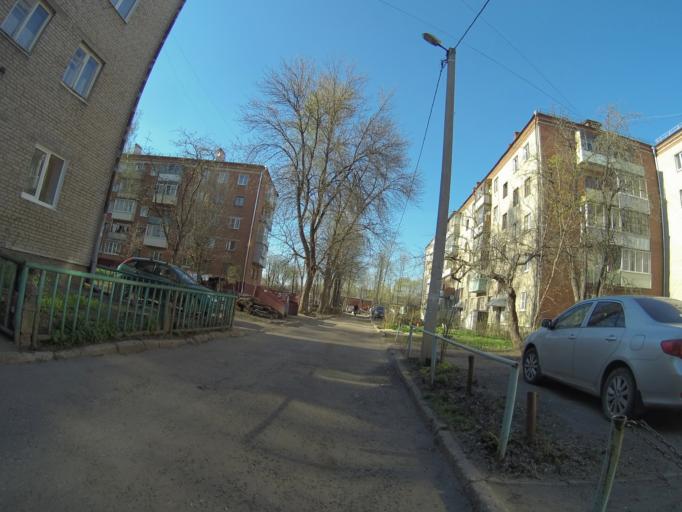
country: RU
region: Vladimir
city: Vladimir
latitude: 56.1499
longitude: 40.4203
